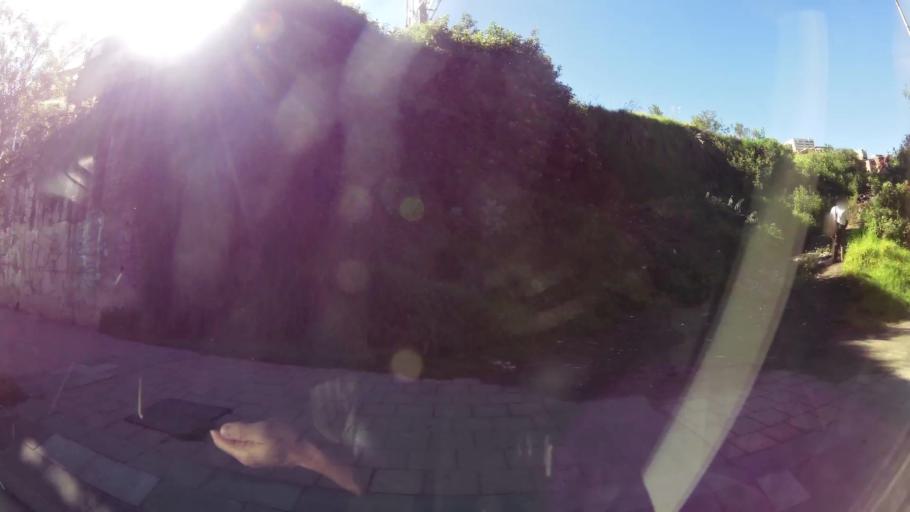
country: EC
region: Pichincha
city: Quito
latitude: -0.1900
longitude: -78.4809
